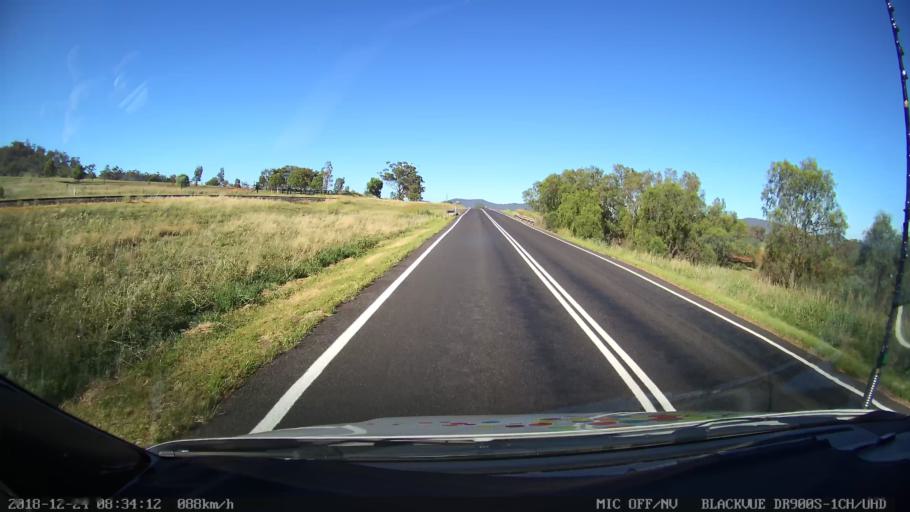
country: AU
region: New South Wales
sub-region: Liverpool Plains
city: Quirindi
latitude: -31.2911
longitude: 150.6737
